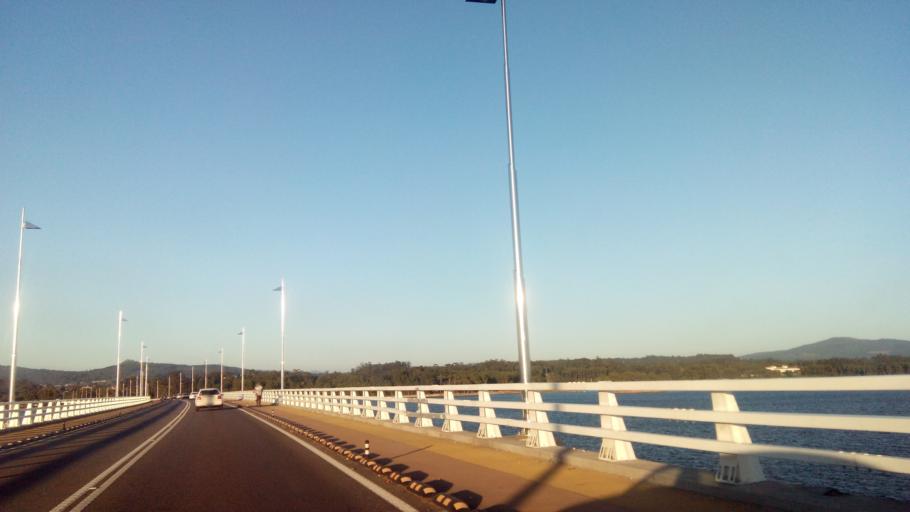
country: ES
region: Galicia
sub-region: Provincia de Pontevedra
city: Vilanova de Arousa
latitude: 42.5463
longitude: -8.8424
